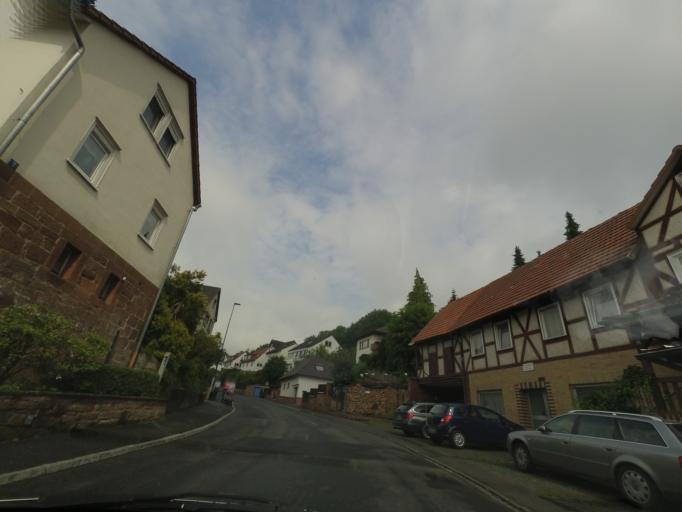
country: DE
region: Hesse
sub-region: Regierungsbezirk Giessen
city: Marburg an der Lahn
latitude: 50.8019
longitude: 8.7468
